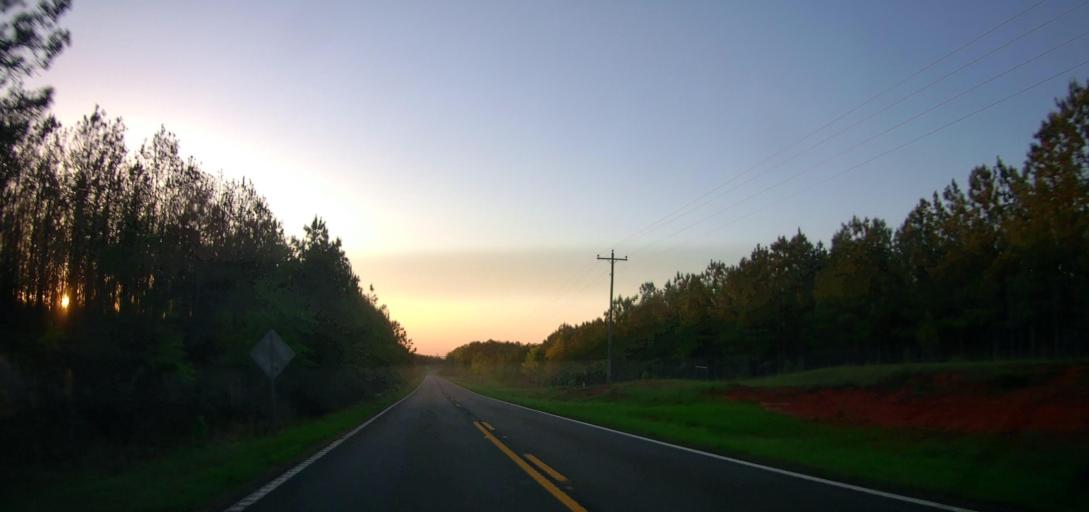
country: US
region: Georgia
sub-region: Marion County
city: Buena Vista
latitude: 32.3910
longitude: -84.5682
